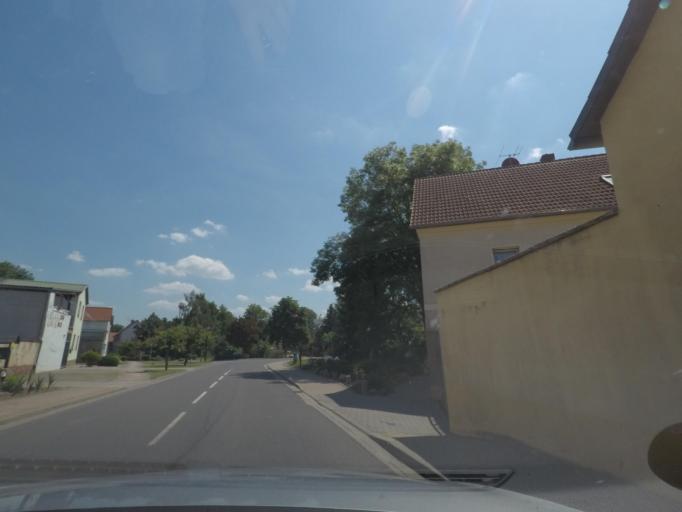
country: DE
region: Saxony-Anhalt
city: Eichenbarleben
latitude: 52.2127
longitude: 11.3996
